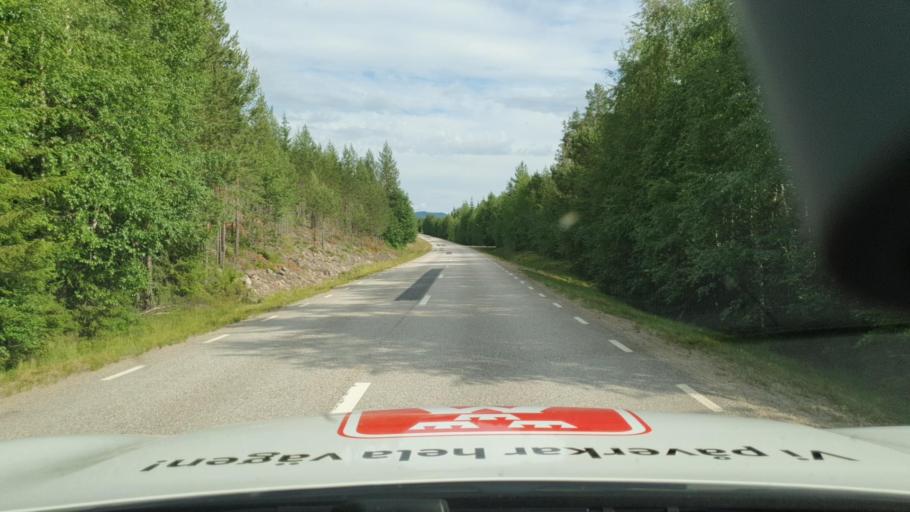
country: NO
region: Hedmark
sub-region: Trysil
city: Innbygda
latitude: 60.9363
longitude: 12.4832
